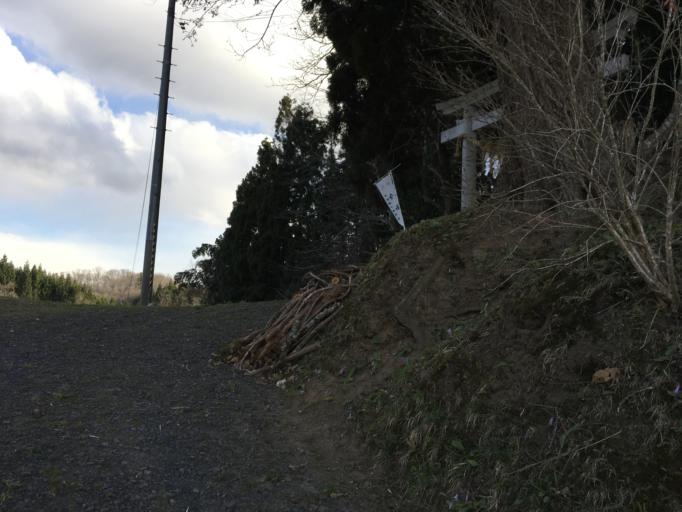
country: JP
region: Iwate
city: Ichinoseki
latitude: 38.9140
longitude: 141.0959
